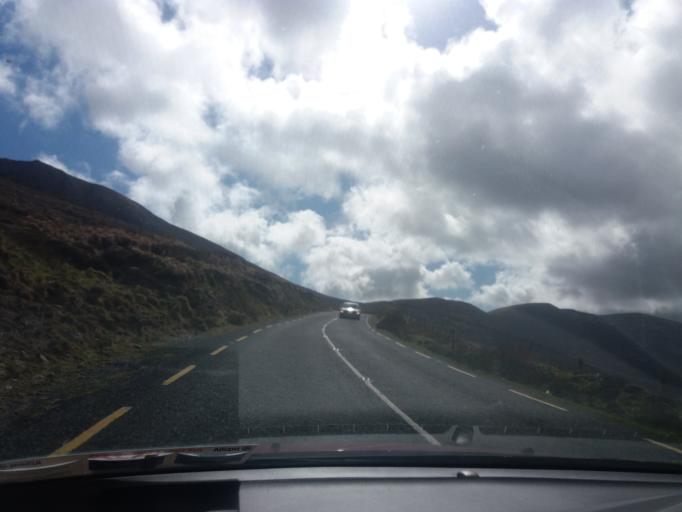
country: IE
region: Munster
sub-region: Ciarrai
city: Dingle
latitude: 52.1950
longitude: -10.1843
